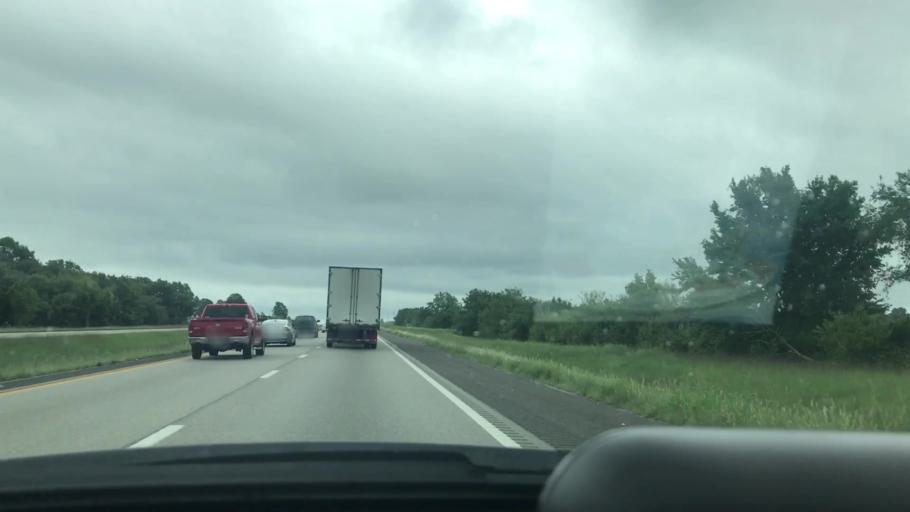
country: US
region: Missouri
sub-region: Christian County
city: Billings
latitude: 37.1863
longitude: -93.6002
